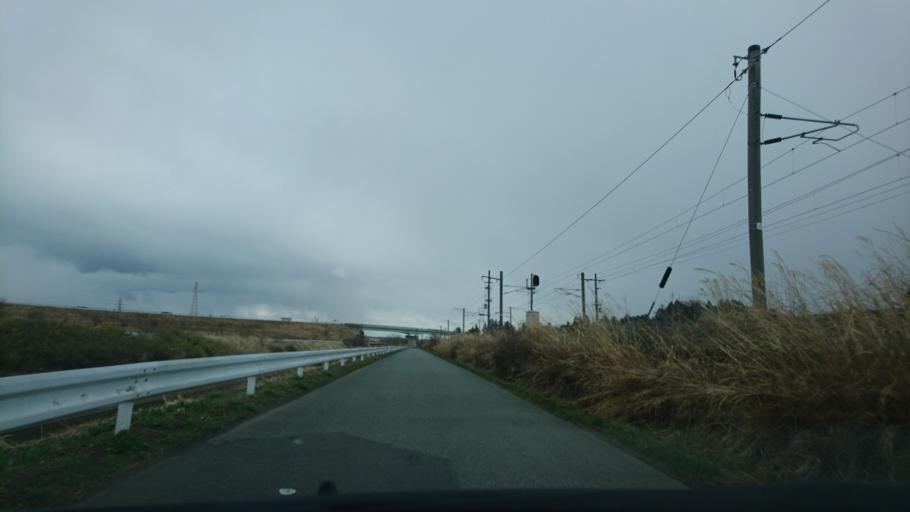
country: JP
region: Iwate
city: Ichinoseki
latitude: 38.9829
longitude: 141.1199
